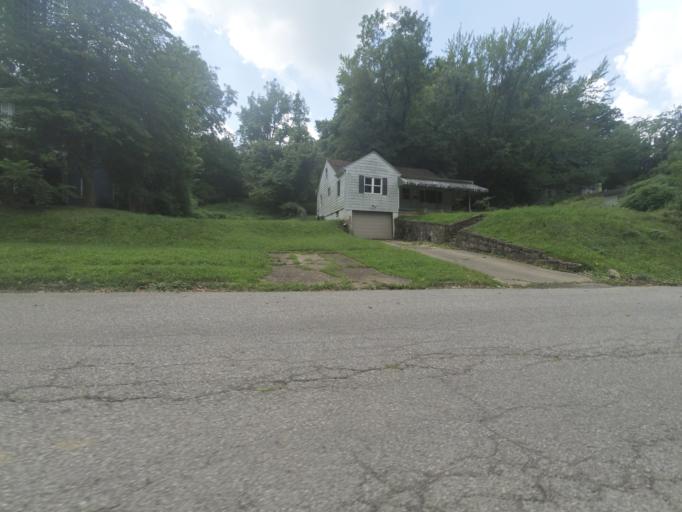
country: US
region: West Virginia
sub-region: Cabell County
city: Huntington
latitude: 38.4173
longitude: -82.4130
